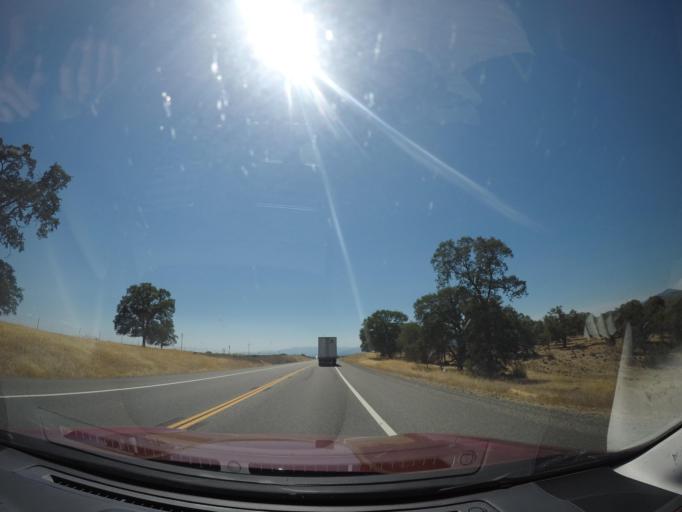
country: US
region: California
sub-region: Shasta County
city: Bella Vista
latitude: 40.6896
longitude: -122.1199
